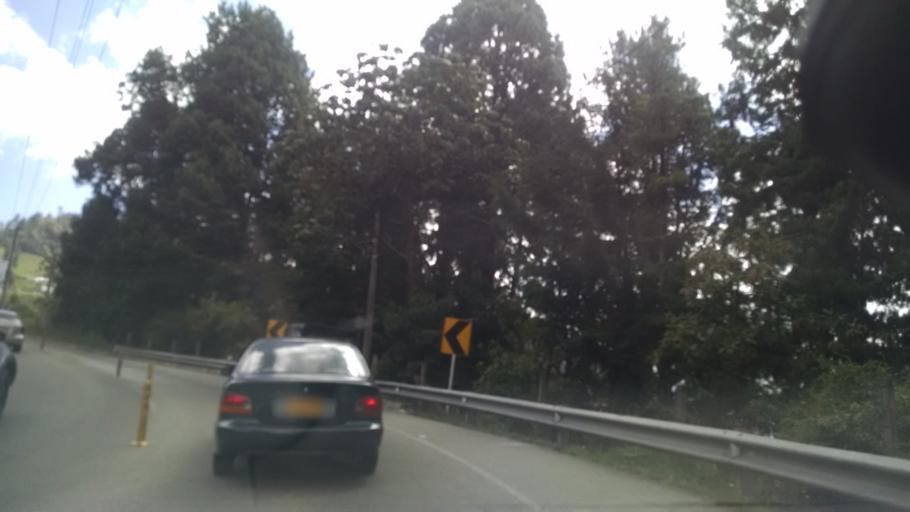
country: CO
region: Antioquia
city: Envigado
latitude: 6.1568
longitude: -75.5471
